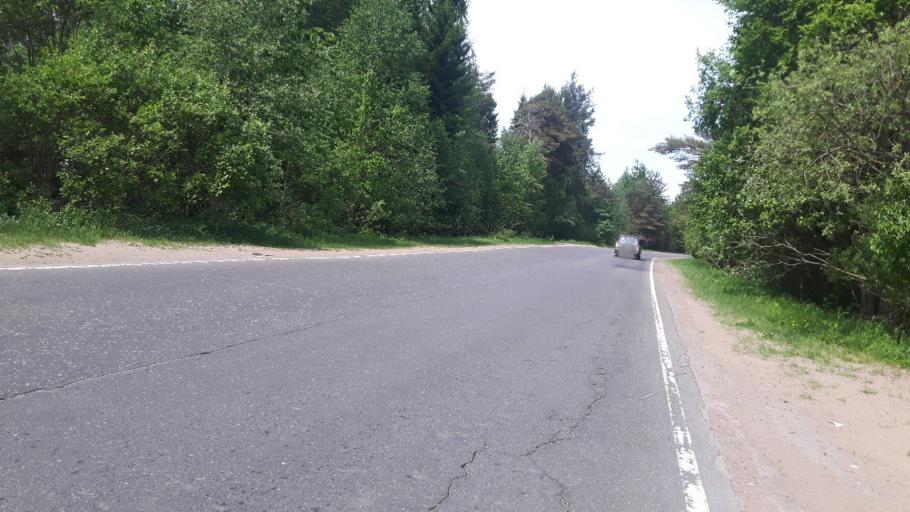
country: RU
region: Leningrad
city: Ust'-Luga
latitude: 59.6479
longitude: 28.2642
